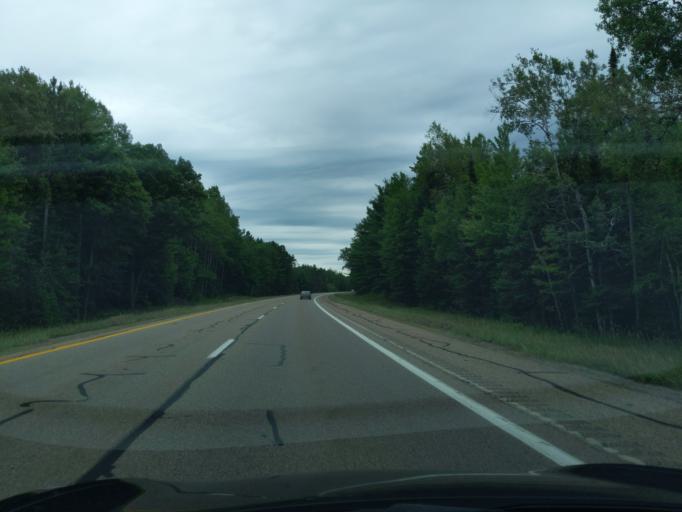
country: US
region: Michigan
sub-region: Roscommon County
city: Houghton Lake
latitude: 44.2253
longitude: -84.7975
